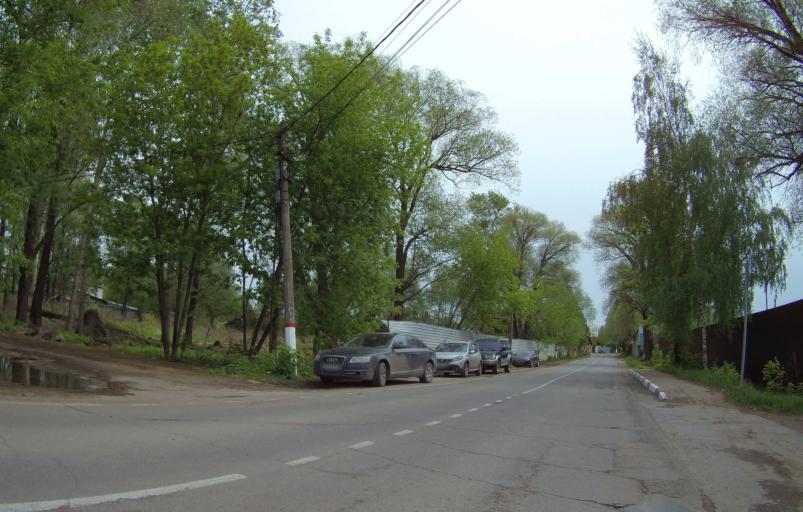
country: RU
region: Moskovskaya
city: Ramenskoye
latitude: 55.5629
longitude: 38.2267
